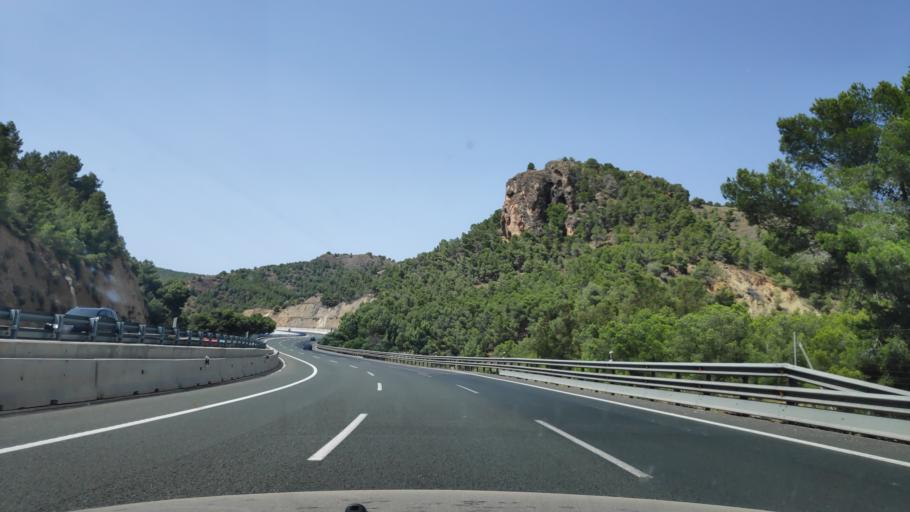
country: ES
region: Murcia
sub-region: Murcia
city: Murcia
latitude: 37.8987
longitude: -1.1420
